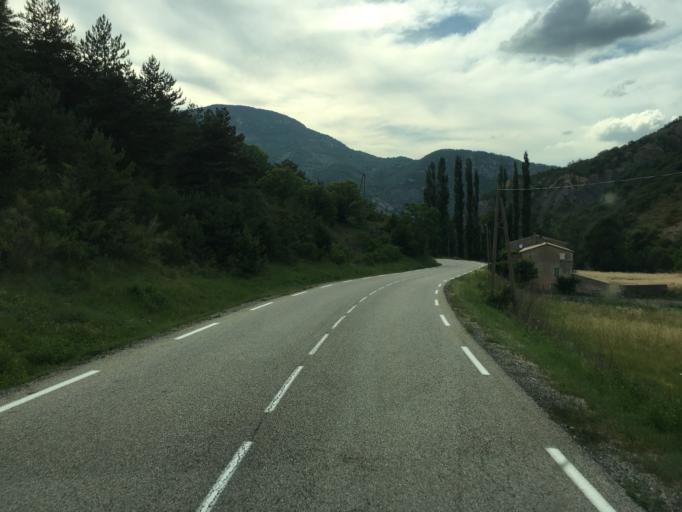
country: FR
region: Rhone-Alpes
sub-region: Departement de la Drome
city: Buis-les-Baronnies
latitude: 44.3926
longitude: 5.3662
